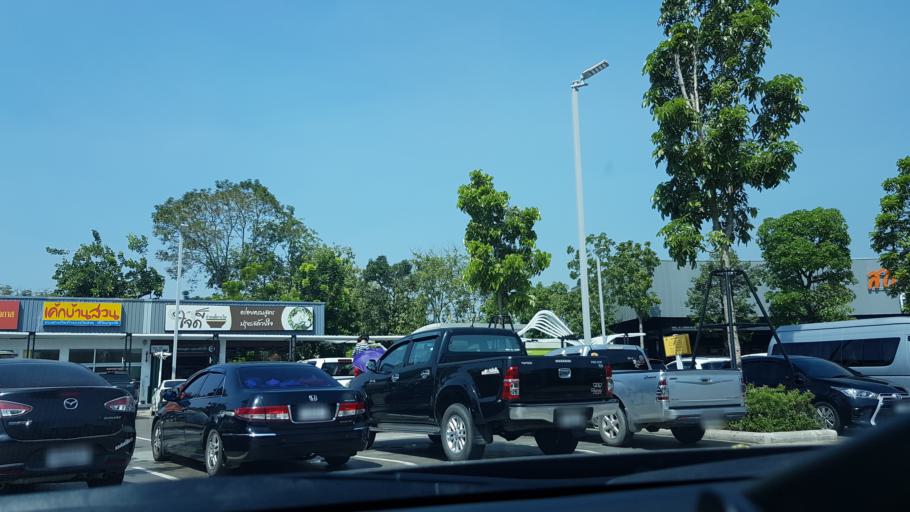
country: TH
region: Sara Buri
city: Nong Khae
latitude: 14.2890
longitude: 100.8175
